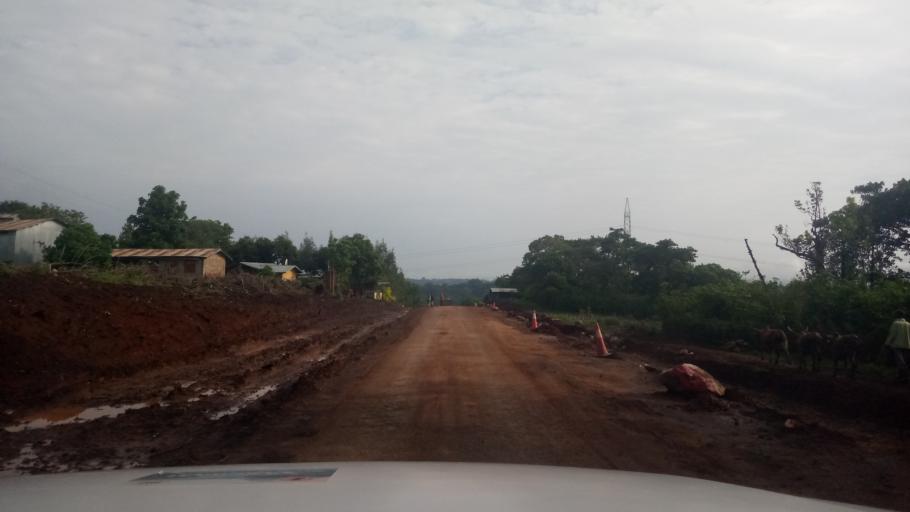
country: ET
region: Oromiya
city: Agaro
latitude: 7.8520
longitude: 36.6549
